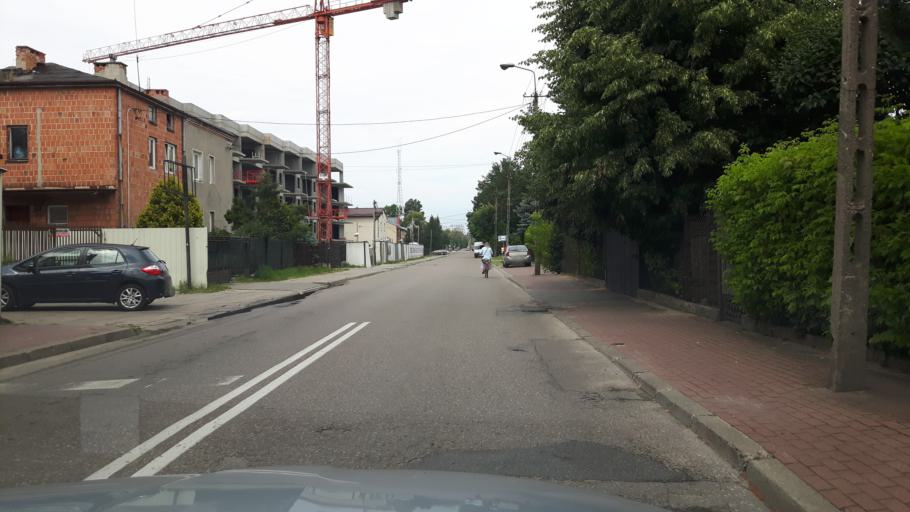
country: PL
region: Masovian Voivodeship
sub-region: Powiat wolominski
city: Wolomin
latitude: 52.3458
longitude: 21.2294
